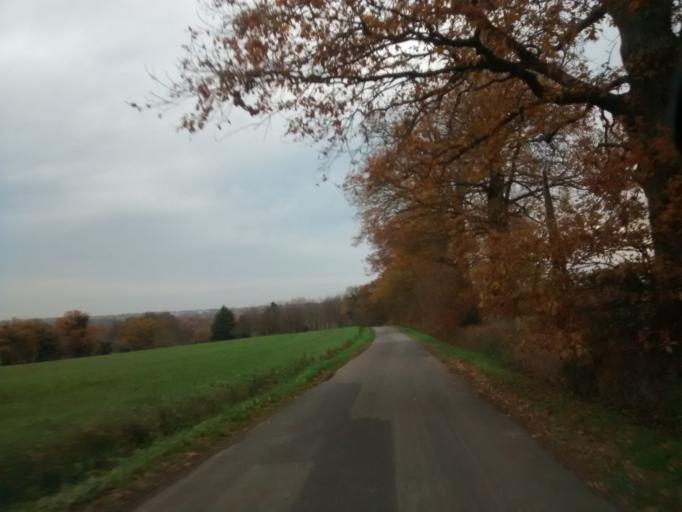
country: FR
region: Brittany
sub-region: Departement d'Ille-et-Vilaine
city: Acigne
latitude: 48.1198
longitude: -1.5616
